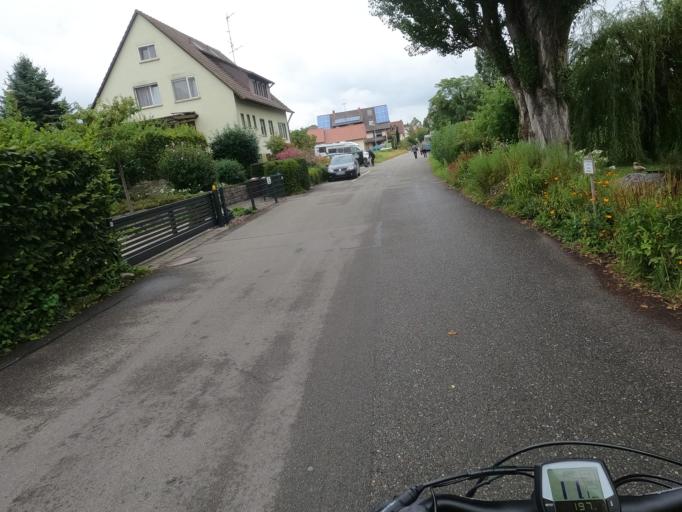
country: DE
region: Baden-Wuerttemberg
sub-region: Freiburg Region
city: Reichenau
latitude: 47.6911
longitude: 9.0802
